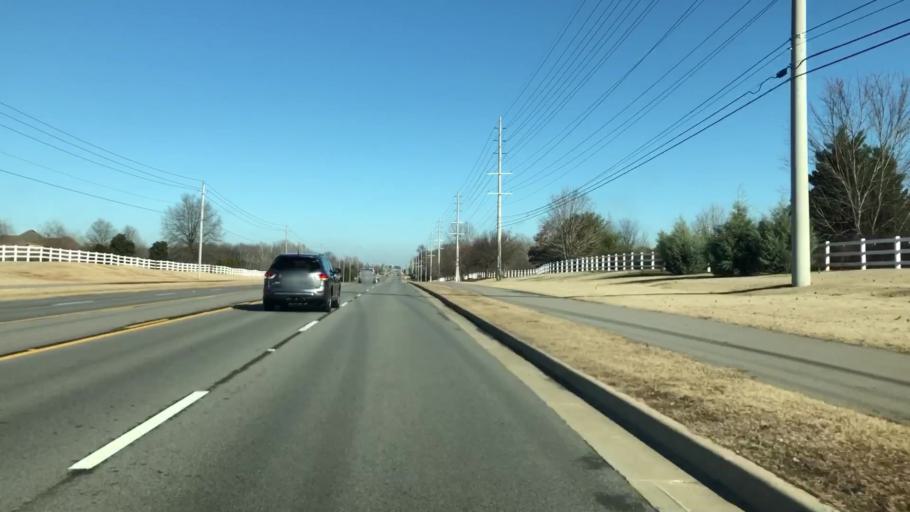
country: US
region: Alabama
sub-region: Madison County
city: Madison
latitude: 34.7108
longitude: -86.7864
